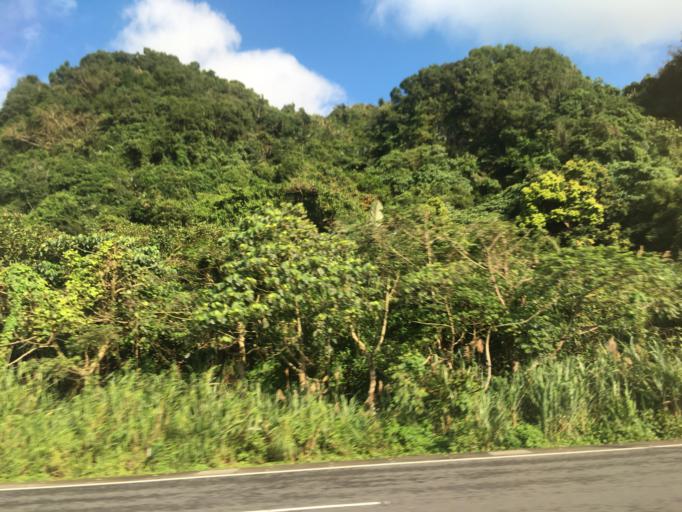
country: TW
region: Taiwan
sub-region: Yilan
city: Yilan
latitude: 24.8968
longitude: 121.8607
